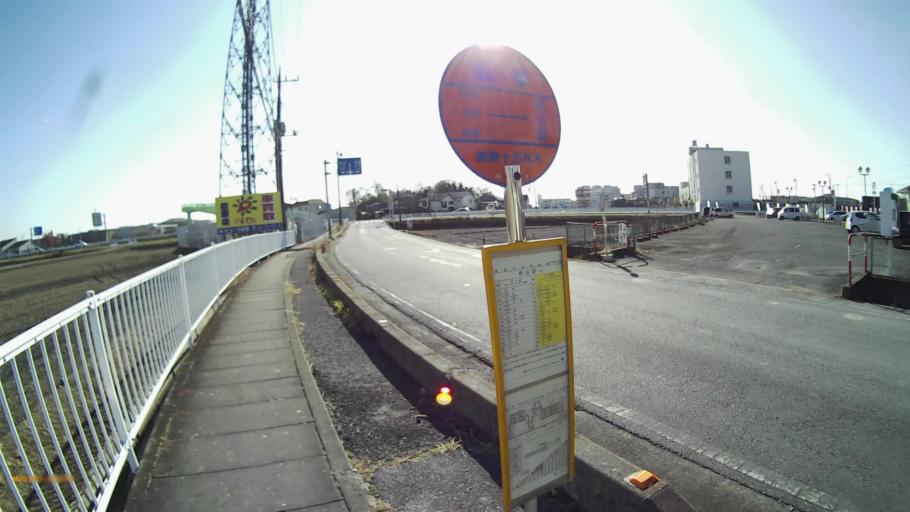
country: JP
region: Saitama
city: Kumagaya
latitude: 36.1723
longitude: 139.3470
